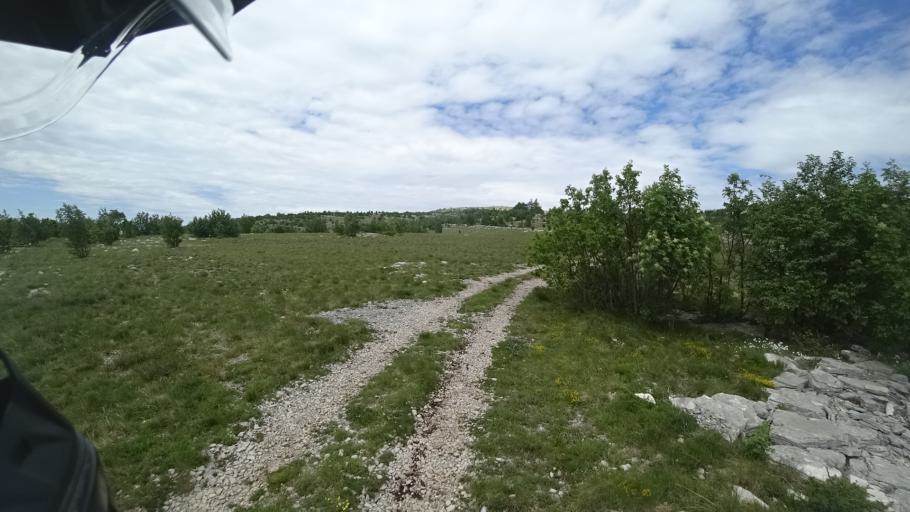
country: HR
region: Splitsko-Dalmatinska
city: Hrvace
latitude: 43.8877
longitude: 16.5883
